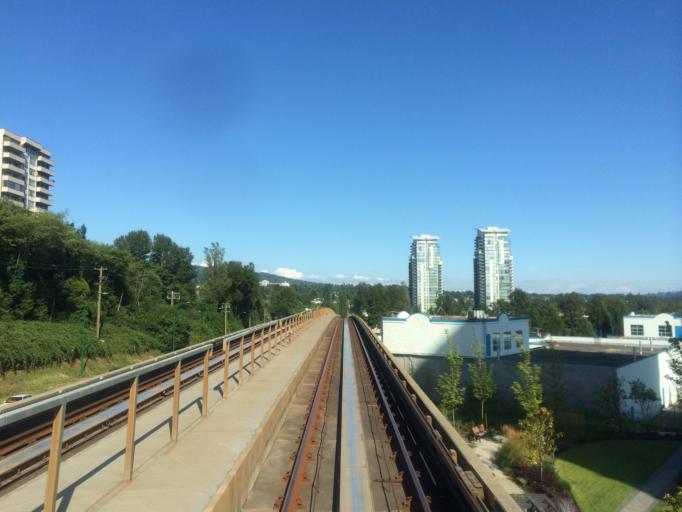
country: CA
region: British Columbia
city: Burnaby
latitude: 49.2649
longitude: -122.9895
